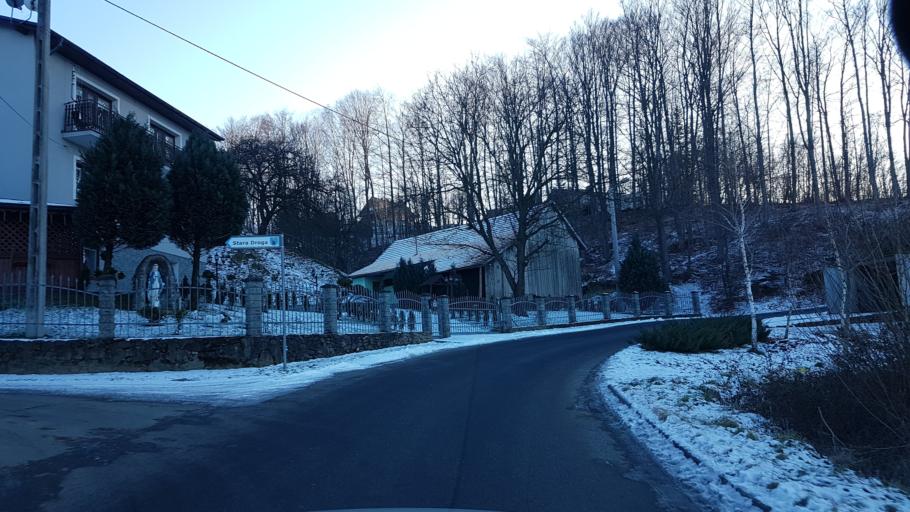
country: PL
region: Lesser Poland Voivodeship
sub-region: Powiat nowosadecki
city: Rytro
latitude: 49.5187
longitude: 20.6632
